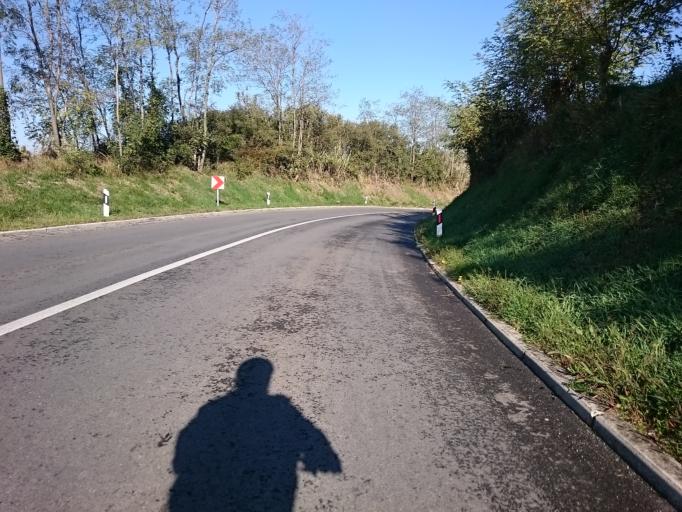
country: HR
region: Istarska
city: Buje
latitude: 45.4003
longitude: 13.6389
